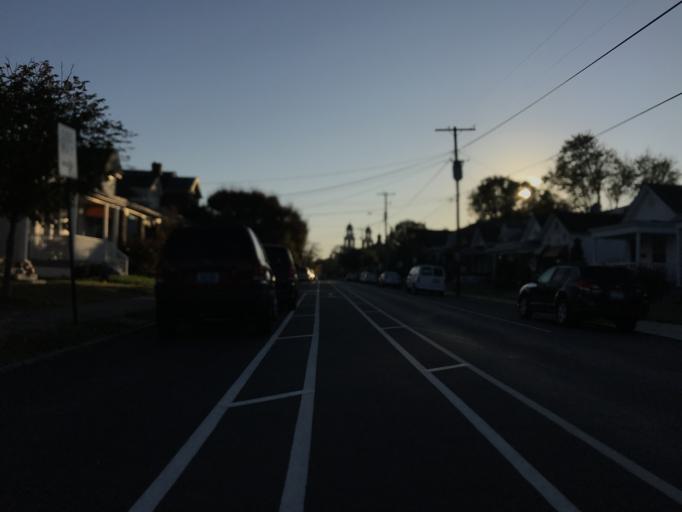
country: US
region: Kentucky
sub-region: Jefferson County
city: Louisville
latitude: 38.2358
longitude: -85.7353
